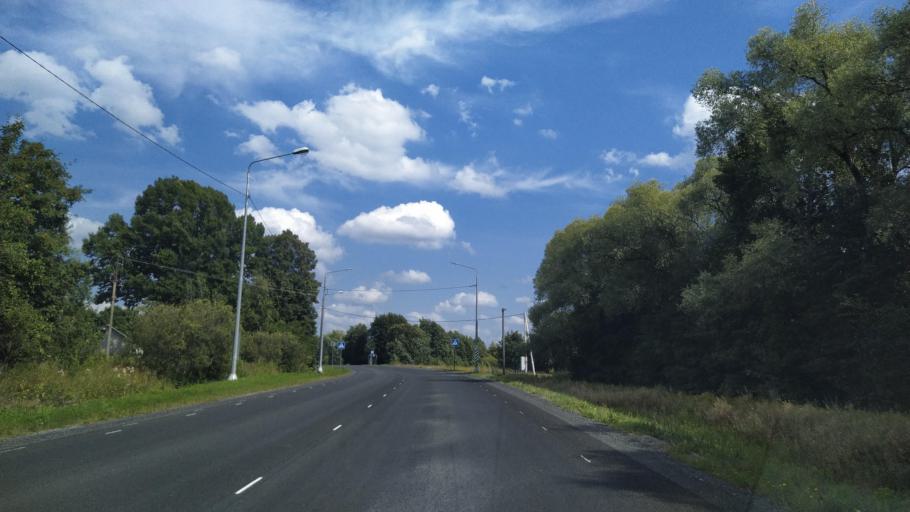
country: RU
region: Pskov
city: Porkhov
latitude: 57.7252
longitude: 29.2716
